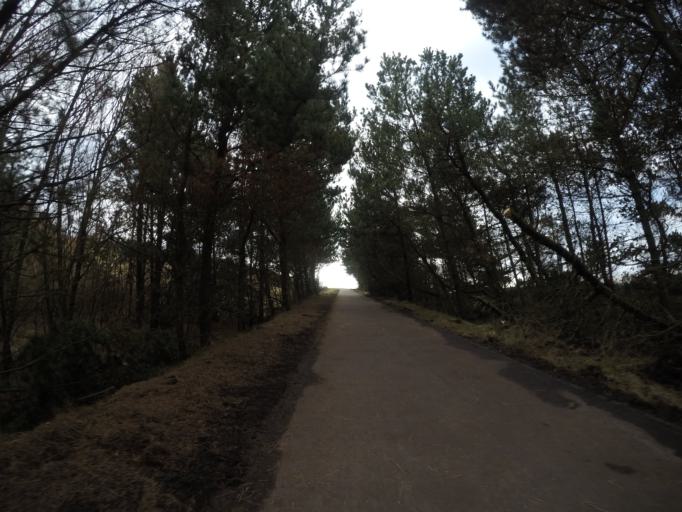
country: GB
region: Scotland
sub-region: North Ayrshire
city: Irvine
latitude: 55.5908
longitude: -4.6684
